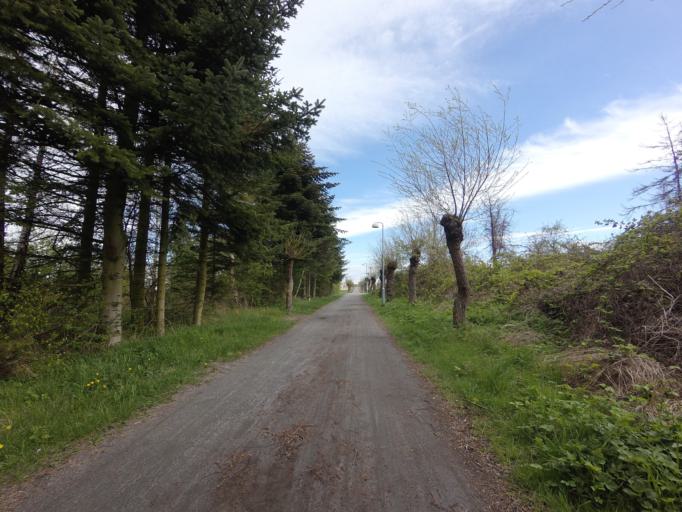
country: SE
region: Skane
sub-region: Malmo
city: Bunkeflostrand
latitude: 55.5563
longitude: 12.9701
